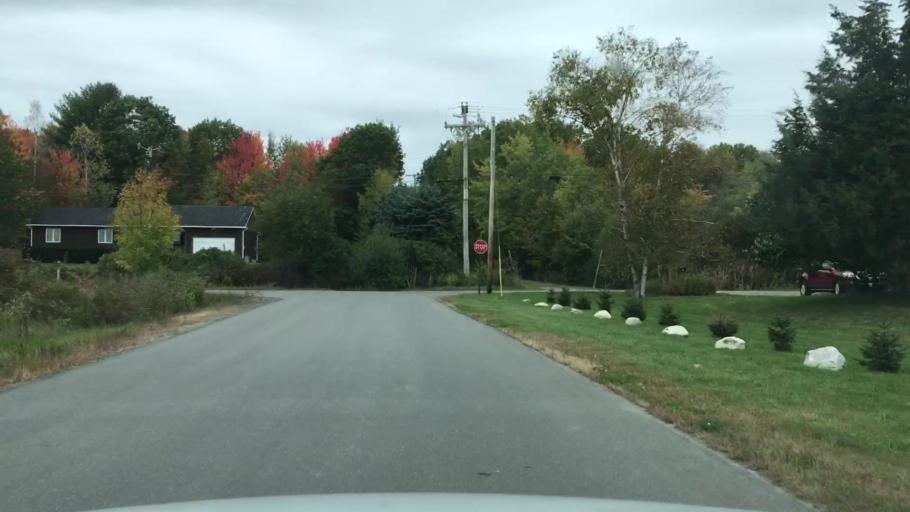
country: US
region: Maine
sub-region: Kennebec County
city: Oakland
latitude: 44.5414
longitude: -69.6869
